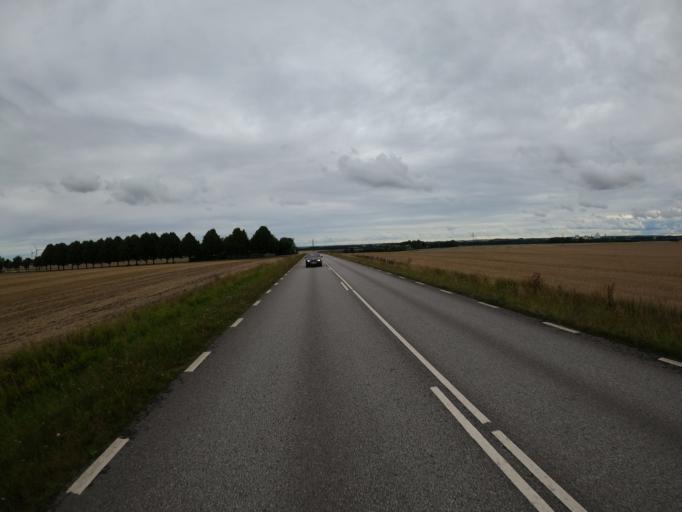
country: SE
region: Skane
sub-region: Lunds Kommun
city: Lund
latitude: 55.7648
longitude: 13.2227
